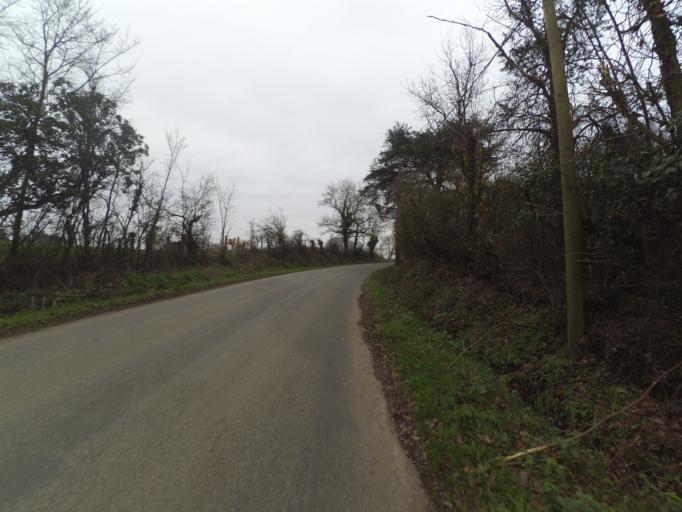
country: FR
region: Pays de la Loire
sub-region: Departement de la Loire-Atlantique
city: Coueron
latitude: 47.2322
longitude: -1.6925
